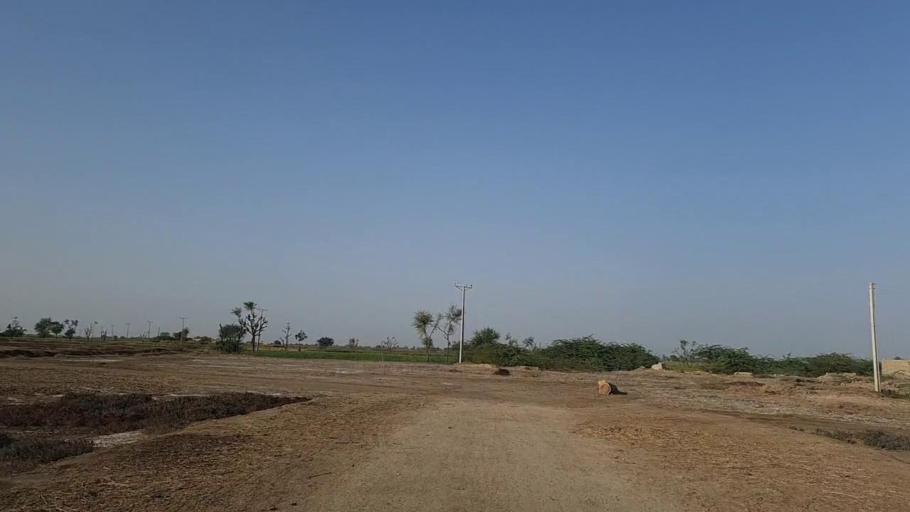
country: PK
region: Sindh
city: Dhoro Naro
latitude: 25.4283
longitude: 69.4851
